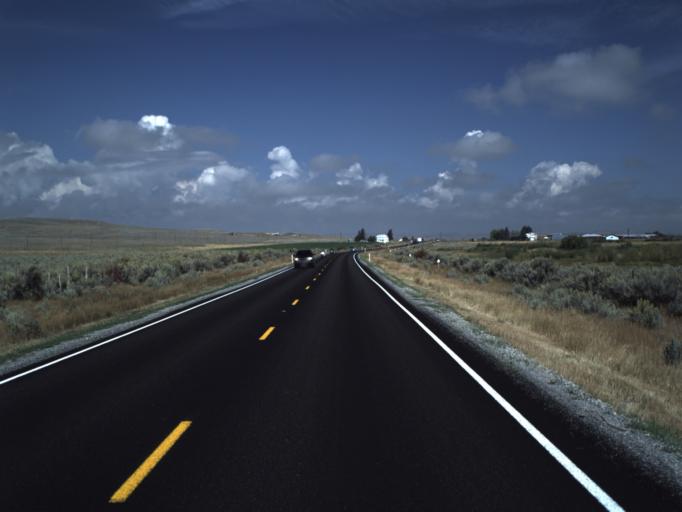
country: US
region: Utah
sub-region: Rich County
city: Randolph
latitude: 41.5921
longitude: -111.1720
